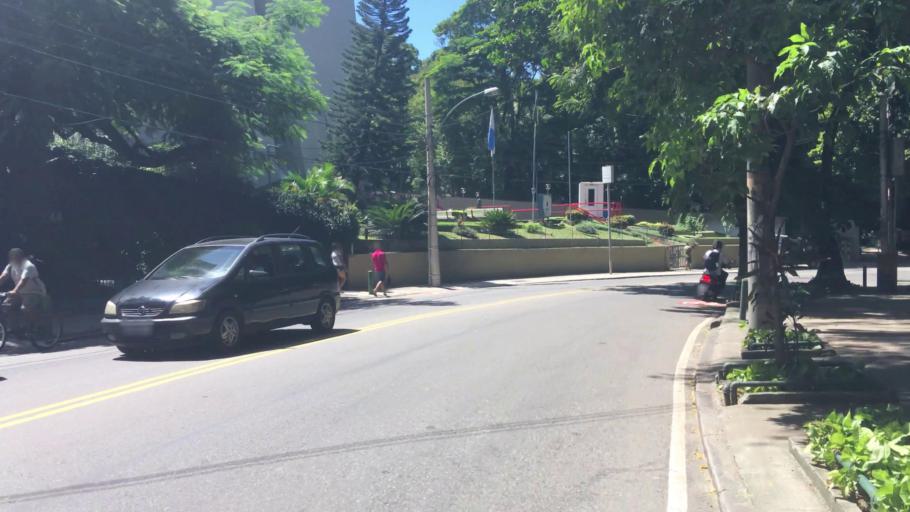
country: BR
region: Rio de Janeiro
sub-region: Rio De Janeiro
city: Rio de Janeiro
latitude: -22.9383
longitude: -43.1958
